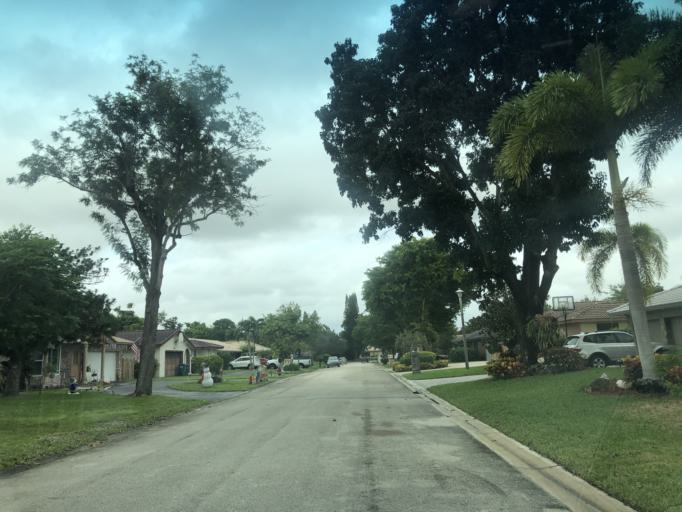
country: US
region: Florida
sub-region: Broward County
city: Coral Springs
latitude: 26.2532
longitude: -80.2414
